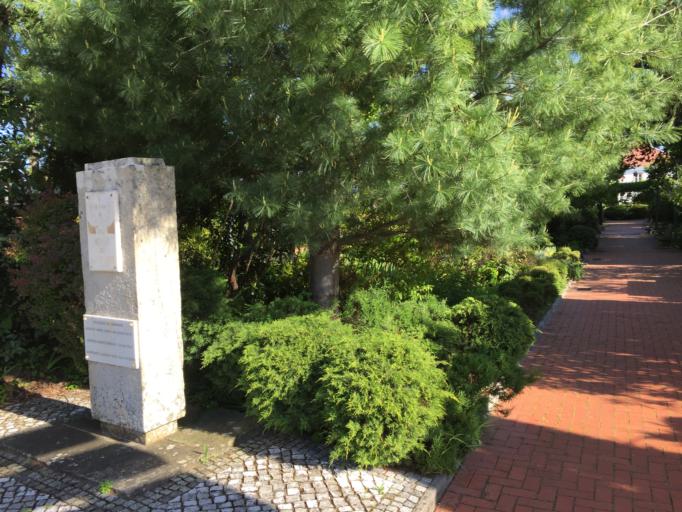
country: PT
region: Leiria
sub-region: Pedrogao Grande
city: Pedrogao Grande
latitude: 39.9190
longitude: -8.1457
